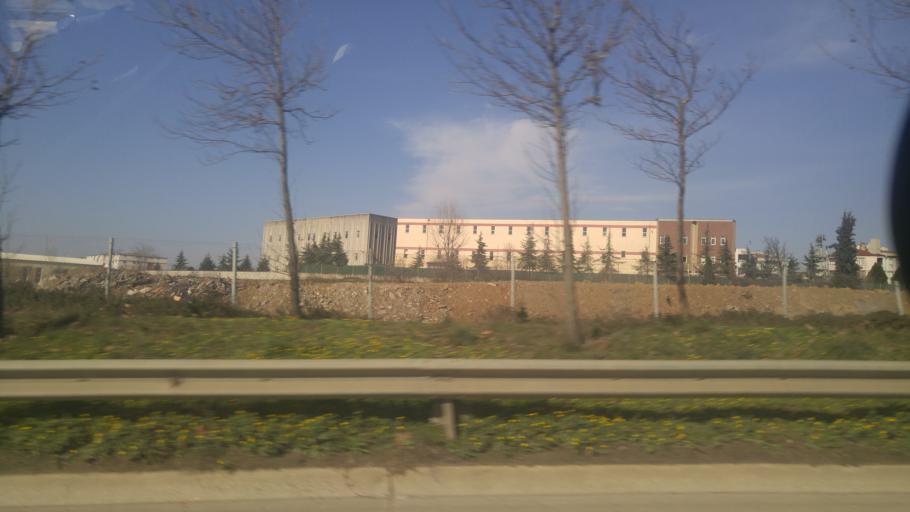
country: TR
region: Kocaeli
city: Balcik
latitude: 40.8564
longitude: 29.3761
